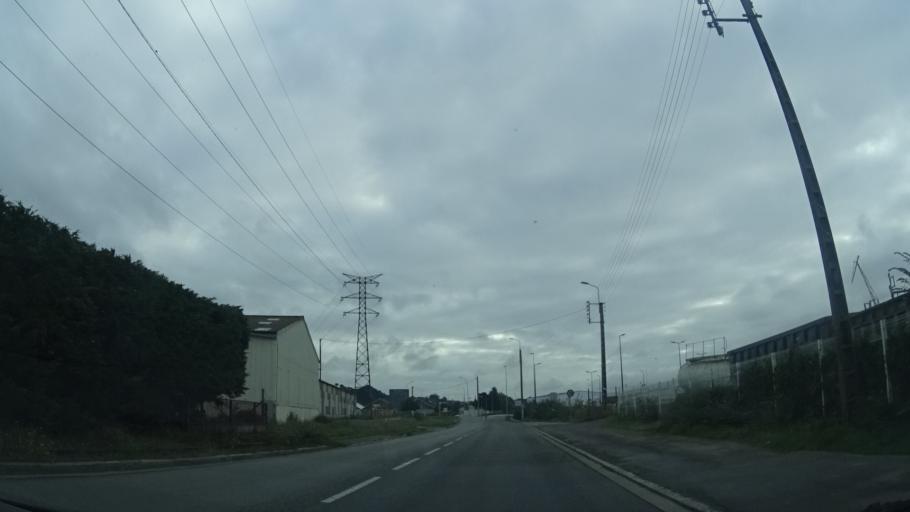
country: FR
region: Brittany
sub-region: Departement du Finistere
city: Brest
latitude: 48.3876
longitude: -4.4615
